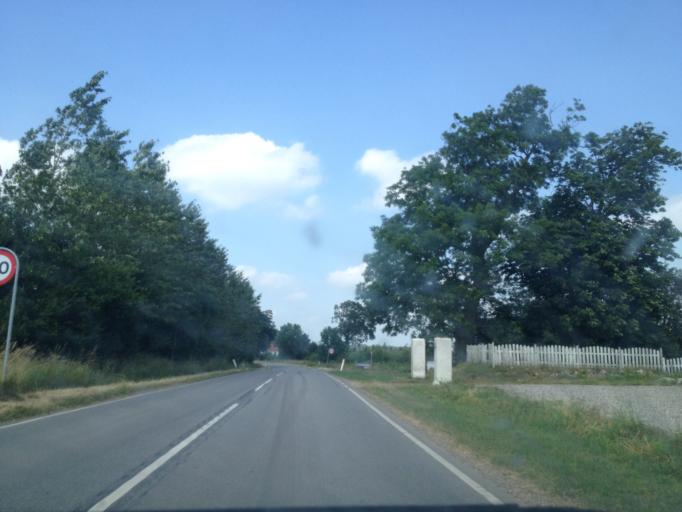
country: DK
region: South Denmark
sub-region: Kolding Kommune
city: Vamdrup
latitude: 55.3758
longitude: 9.2778
